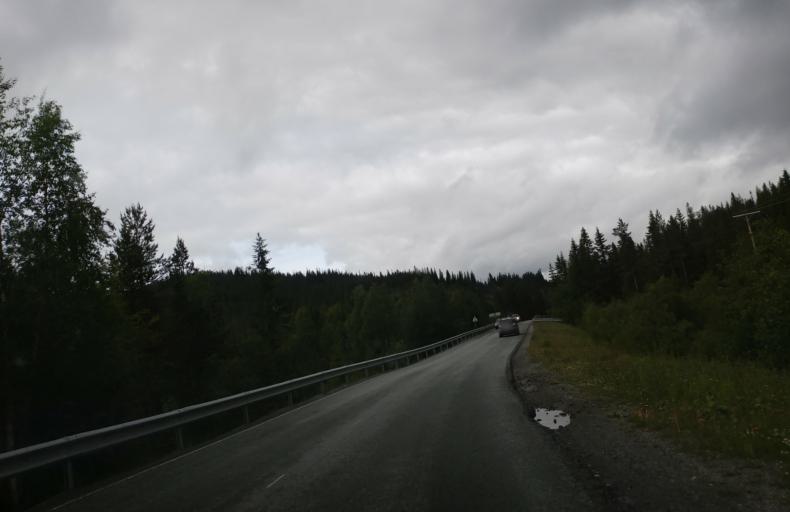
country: NO
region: Sor-Trondelag
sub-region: Selbu
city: Mebonden
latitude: 63.3398
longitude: 11.0799
